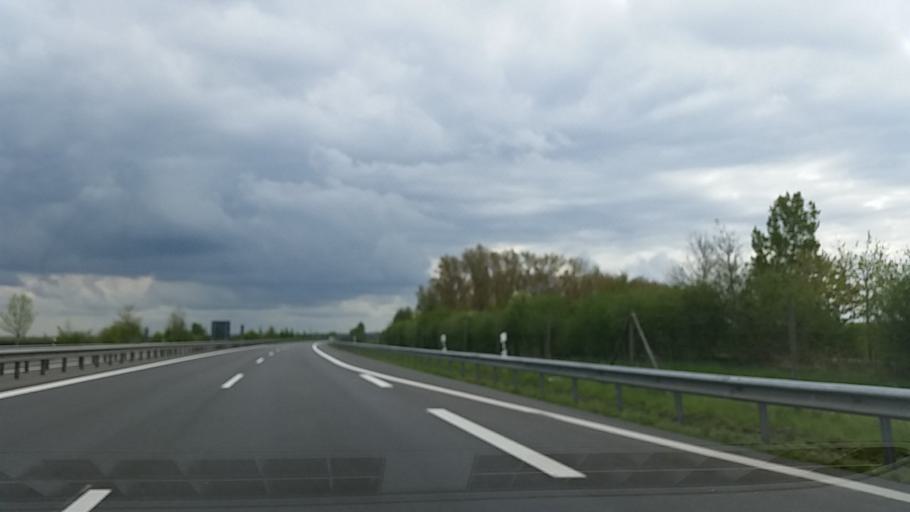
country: DE
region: Lower Saxony
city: Dollern
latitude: 53.5414
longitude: 9.5736
